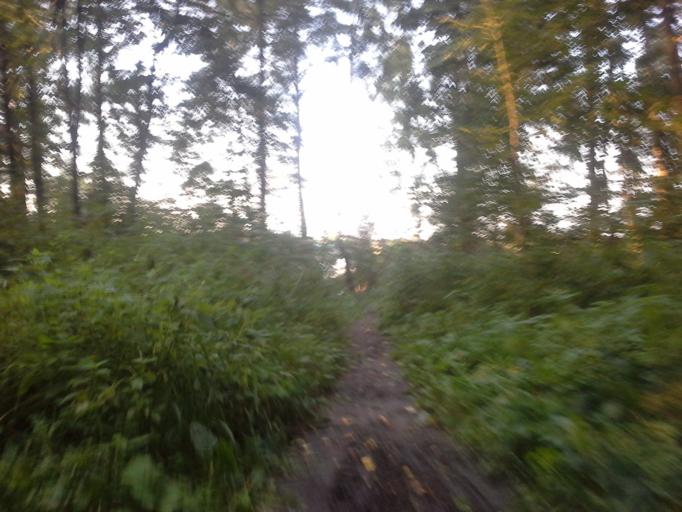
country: RU
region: Moskovskaya
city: Dubrovitsy
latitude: 55.5015
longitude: 37.4395
